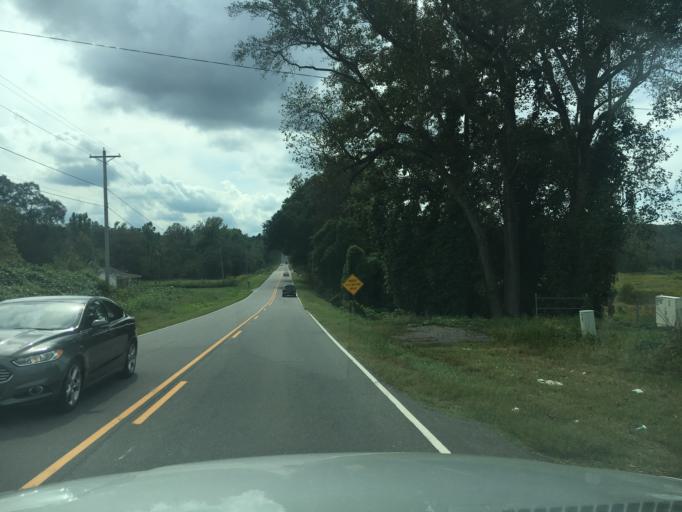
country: US
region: North Carolina
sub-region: Gaston County
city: Dallas
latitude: 35.3040
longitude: -81.2191
